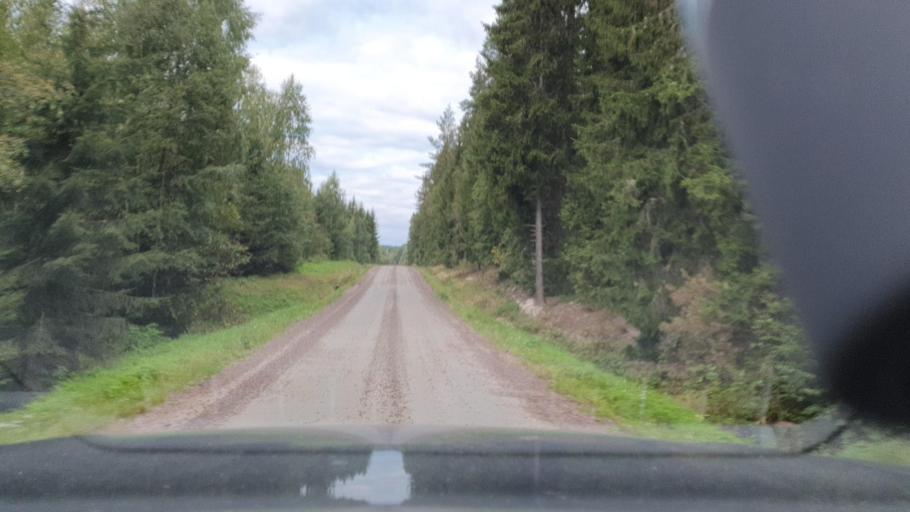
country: SE
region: Vaermland
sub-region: Munkfors Kommun
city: Munkfors
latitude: 59.8916
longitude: 13.4995
